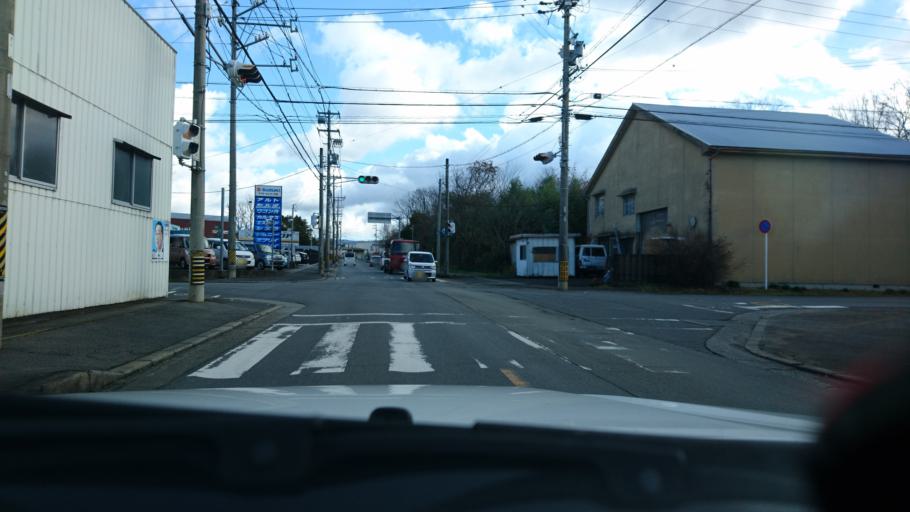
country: JP
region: Mie
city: Ueno-ebisumachi
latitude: 34.7593
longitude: 136.1568
